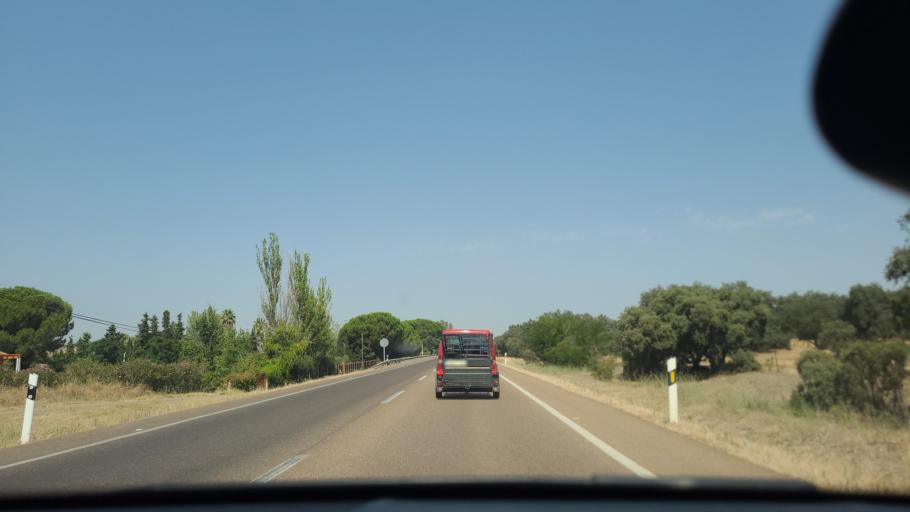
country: ES
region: Extremadura
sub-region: Provincia de Badajoz
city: Badajoz
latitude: 38.8325
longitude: -6.9199
